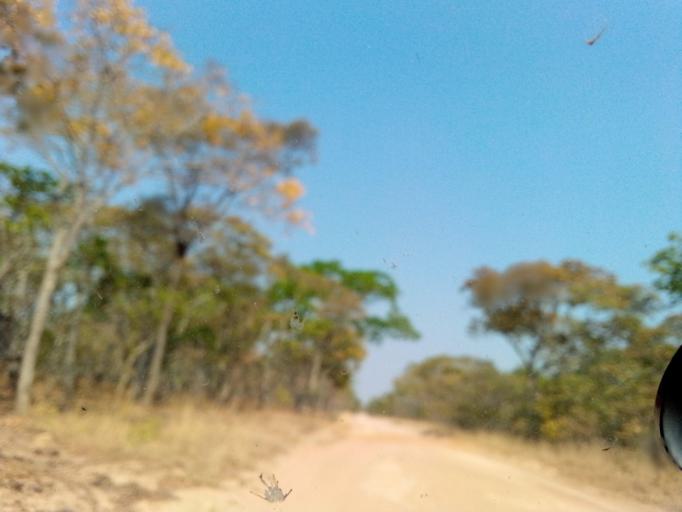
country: ZM
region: Northern
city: Mpika
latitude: -12.2421
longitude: 30.8439
